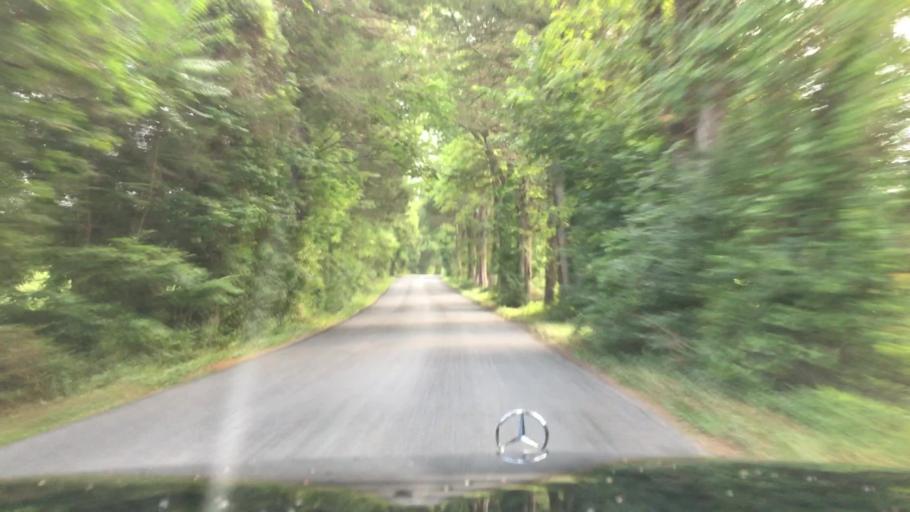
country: US
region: Virginia
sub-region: Campbell County
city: Timberlake
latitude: 37.2611
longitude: -79.3132
